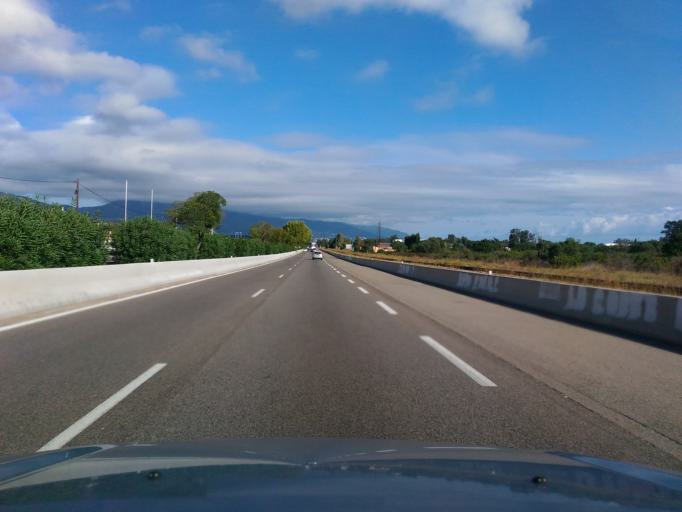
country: FR
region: Corsica
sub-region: Departement de la Haute-Corse
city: Biguglia
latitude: 42.6014
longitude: 9.4385
